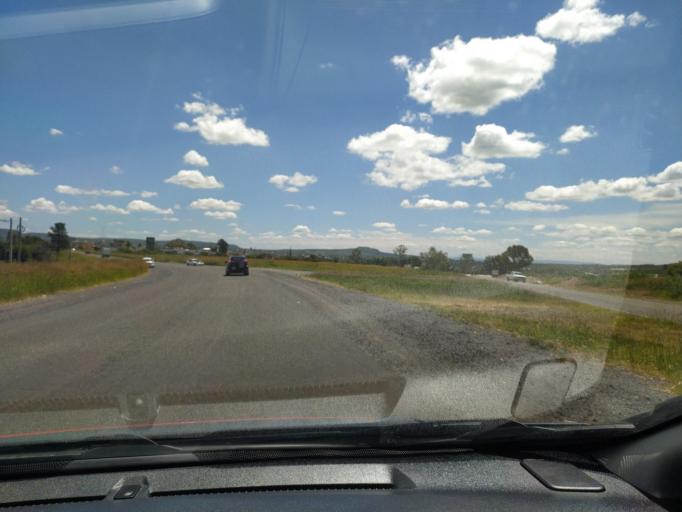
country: MX
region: Jalisco
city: San Diego de Alejandria
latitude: 20.9997
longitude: -102.0066
